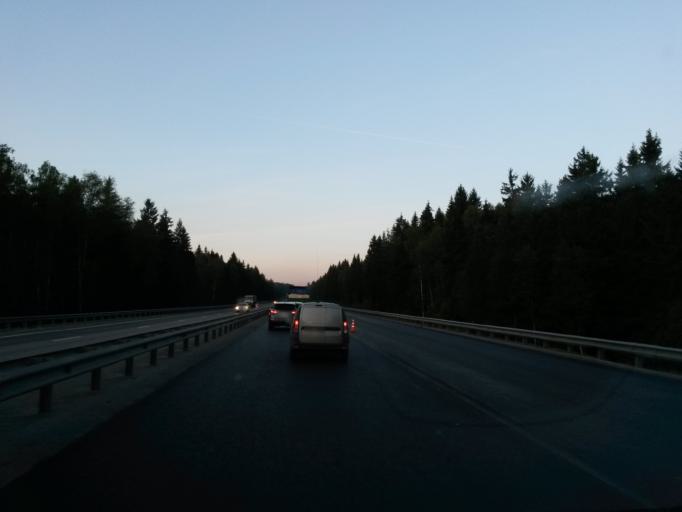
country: RU
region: Moskovskaya
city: Svatkovo
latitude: 56.3144
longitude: 38.2456
